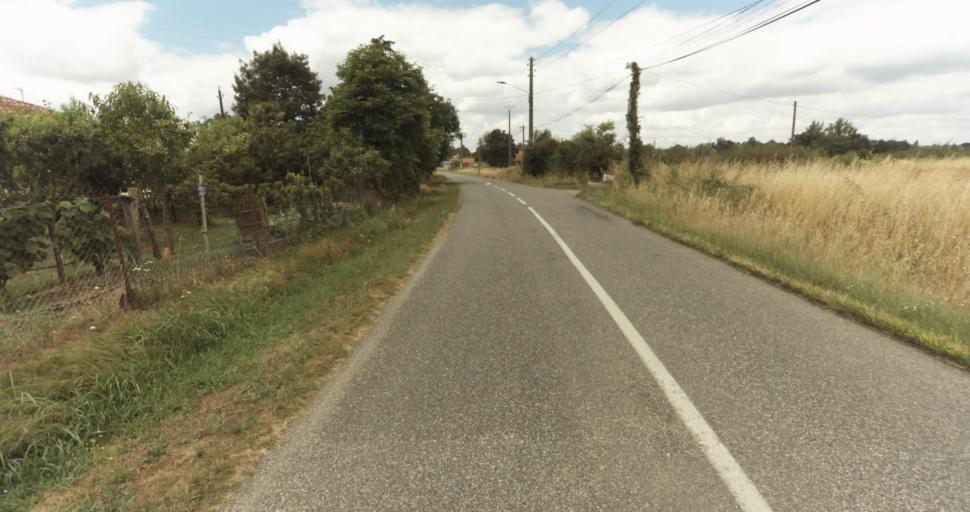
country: FR
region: Midi-Pyrenees
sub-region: Departement de la Haute-Garonne
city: Fontenilles
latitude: 43.5499
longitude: 1.2084
